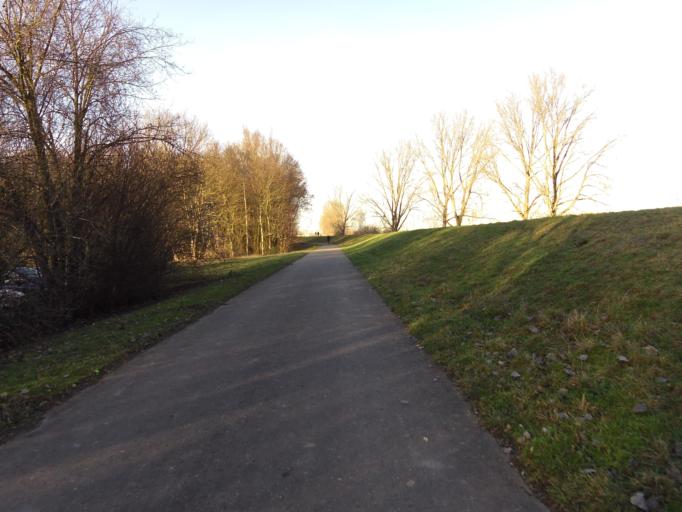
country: DE
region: Rheinland-Pfalz
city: Frankenthal
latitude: 49.5552
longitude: 8.4115
